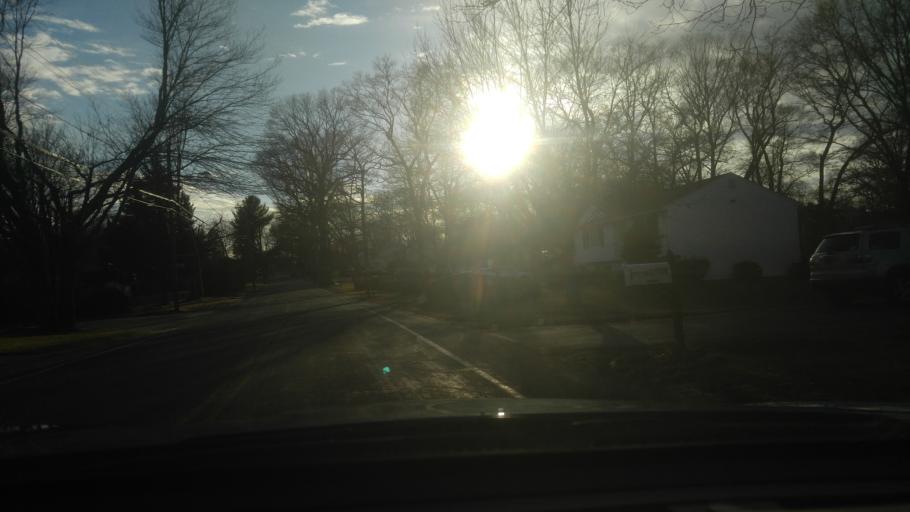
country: US
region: Rhode Island
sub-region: Washington County
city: Exeter
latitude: 41.5883
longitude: -71.4946
